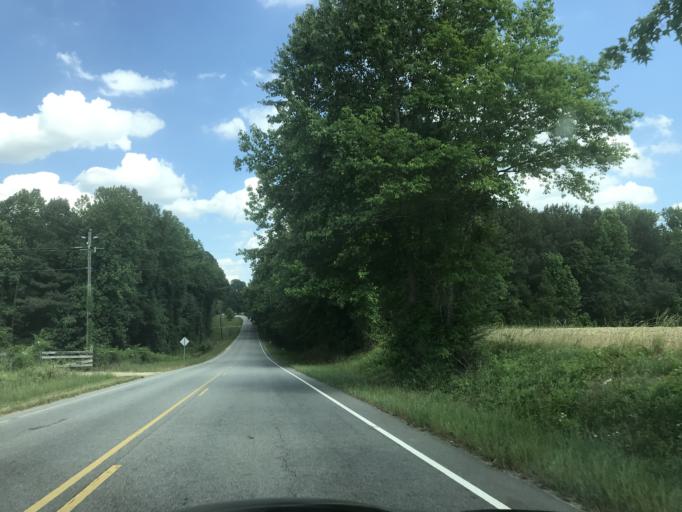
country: US
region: North Carolina
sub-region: Nash County
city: Spring Hope
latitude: 35.9202
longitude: -78.1719
